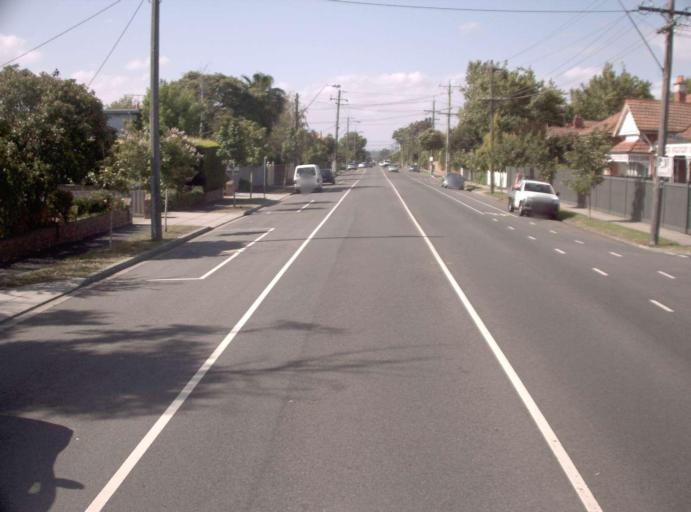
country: AU
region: Victoria
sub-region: Stonnington
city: Malvern East
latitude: -37.8700
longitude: 145.0390
